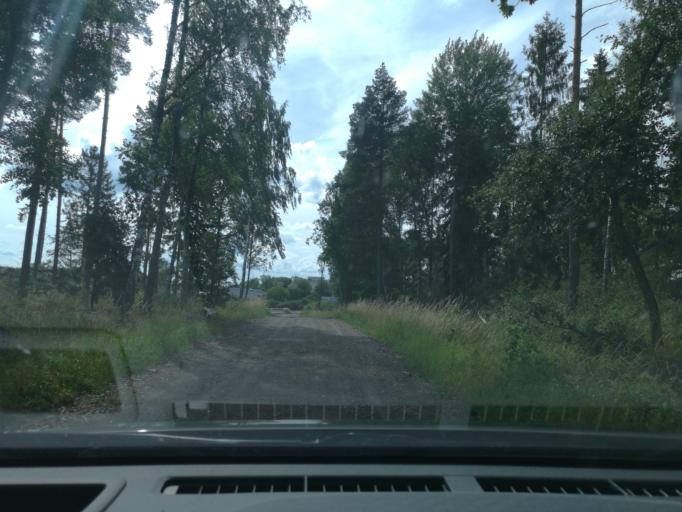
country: SE
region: Stockholm
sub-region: Sigtuna Kommun
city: Marsta
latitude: 59.6080
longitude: 17.8018
